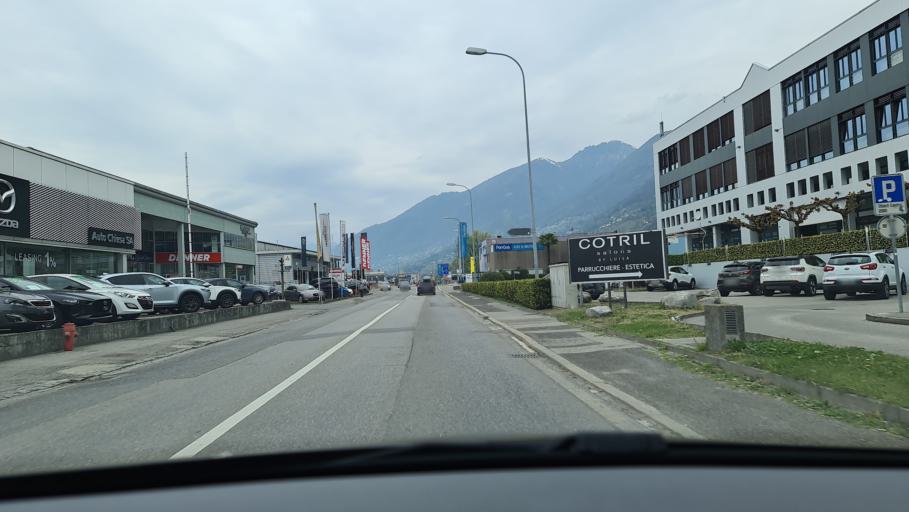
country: CH
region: Ticino
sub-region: Locarno District
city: Gordola
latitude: 46.1757
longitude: 8.8886
